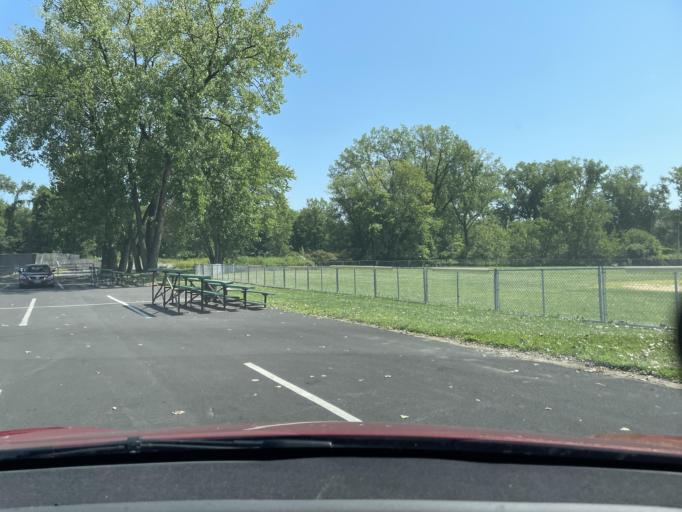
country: US
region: New York
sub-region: Ulster County
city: Kingston
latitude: 41.9356
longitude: -74.0145
